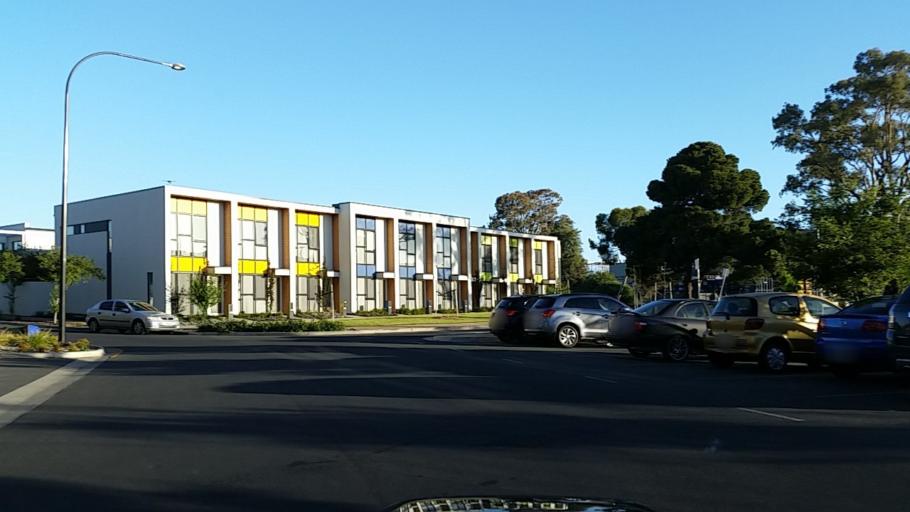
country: AU
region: South Australia
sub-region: Charles Sturt
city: Albert Park
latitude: -34.8704
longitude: 138.5301
